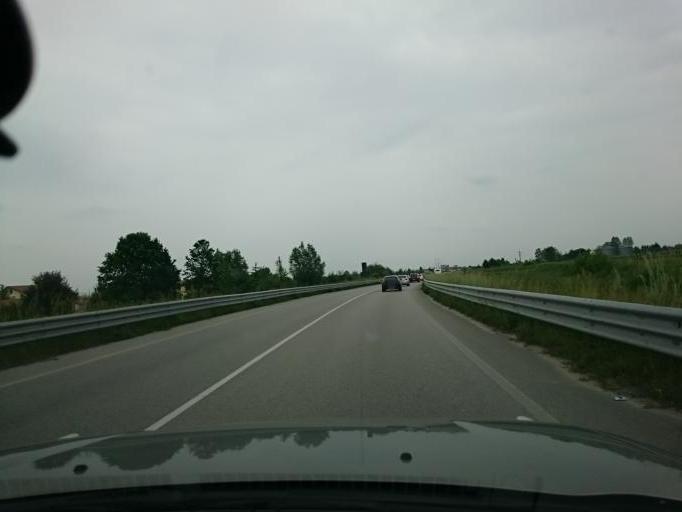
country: IT
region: Veneto
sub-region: Provincia di Padova
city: Montegrotto Terme
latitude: 45.3191
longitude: 11.7976
